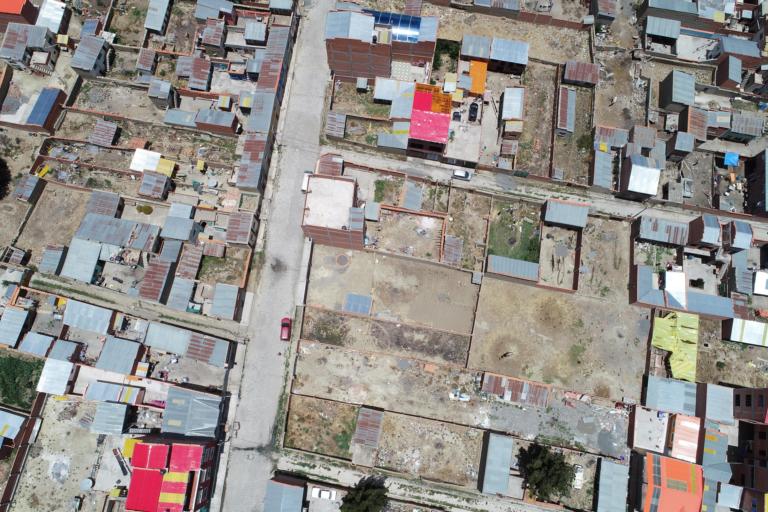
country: BO
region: La Paz
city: Achacachi
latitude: -16.0486
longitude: -68.6856
